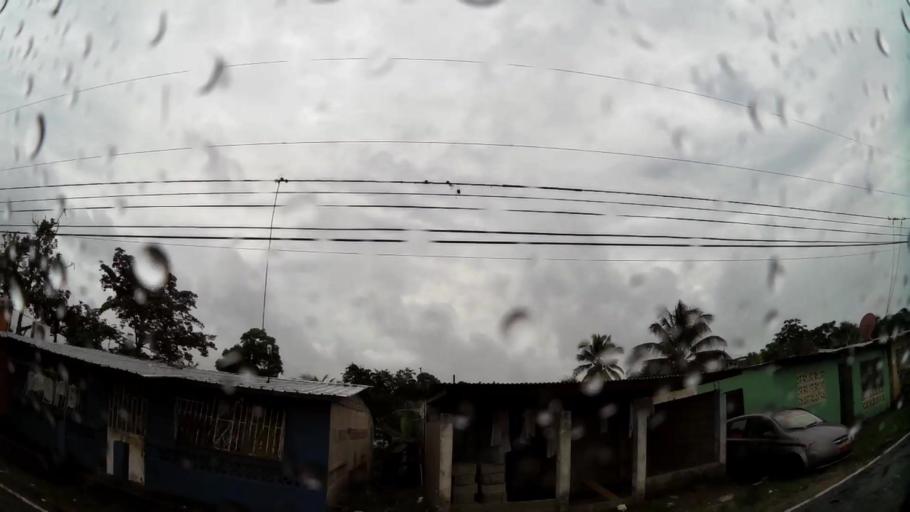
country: PA
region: Colon
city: Arco Iris
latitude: 9.3373
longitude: -79.8696
